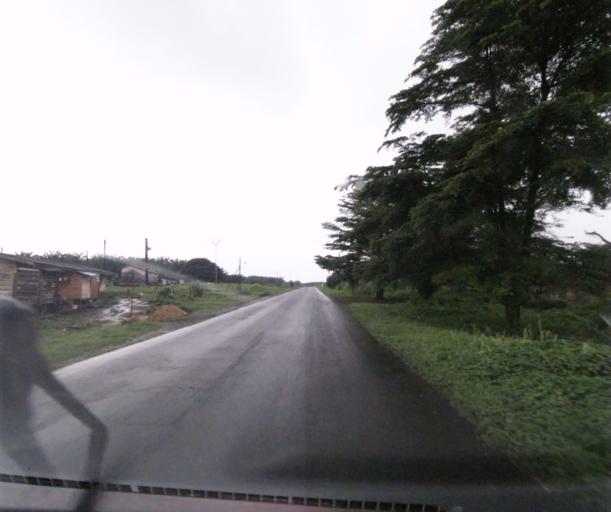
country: CM
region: South-West Province
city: Idenao
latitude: 4.1036
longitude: 8.9896
